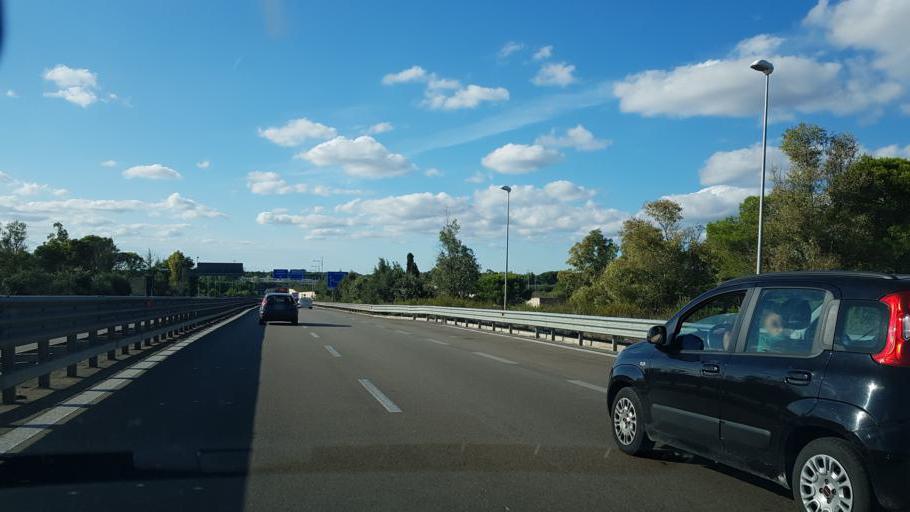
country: IT
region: Apulia
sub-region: Provincia di Lecce
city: Lequile
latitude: 40.3317
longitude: 18.1370
